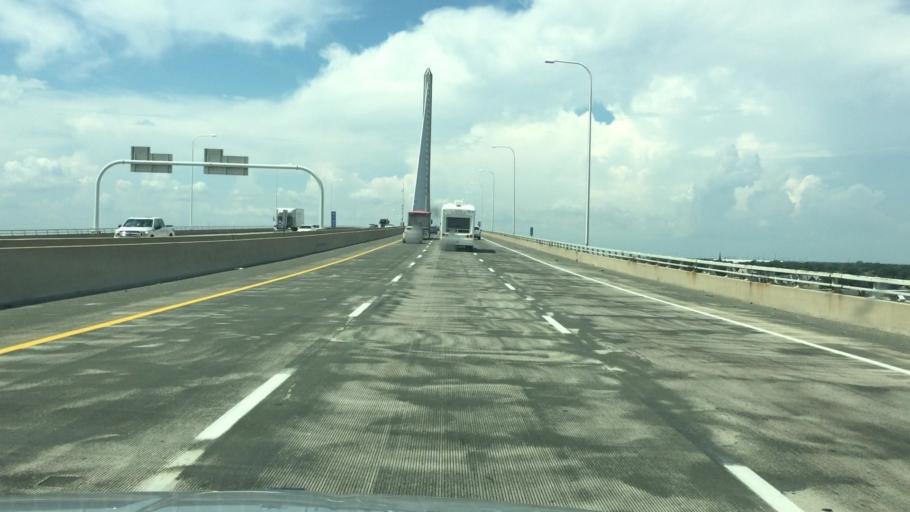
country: US
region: Ohio
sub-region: Lucas County
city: Oregon
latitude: 41.6574
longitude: -83.5090
